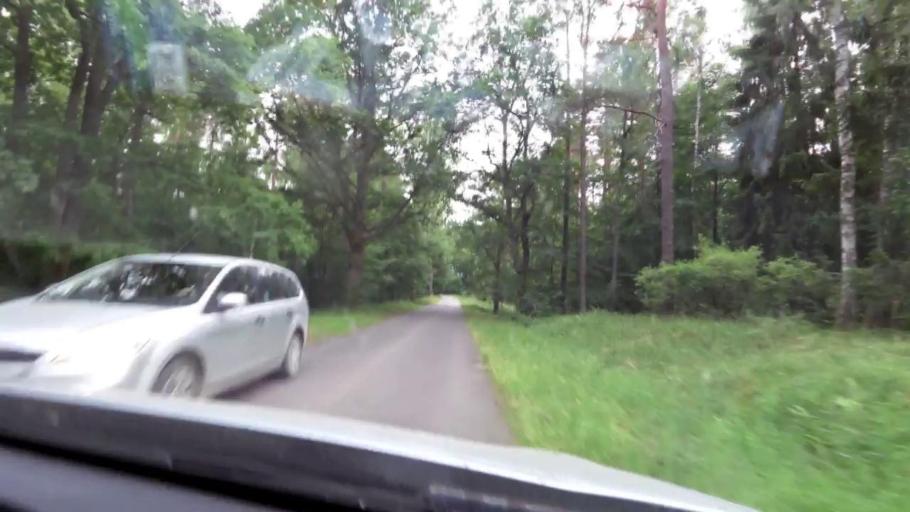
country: PL
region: Pomeranian Voivodeship
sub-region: Powiat bytowski
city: Trzebielino
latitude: 54.2421
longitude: 16.9998
